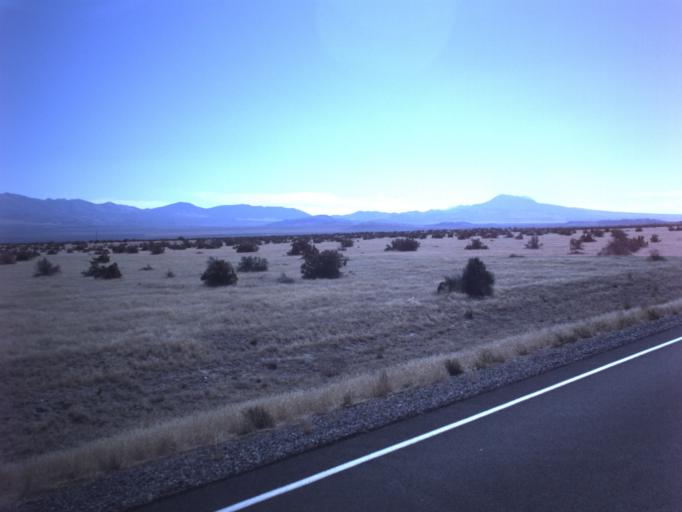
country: US
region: Utah
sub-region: Tooele County
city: Grantsville
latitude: 40.2757
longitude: -112.7416
